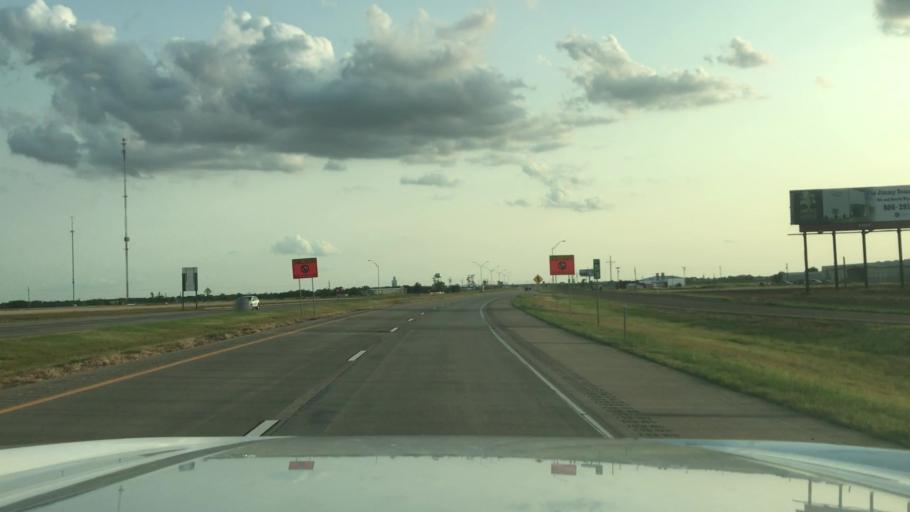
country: US
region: Texas
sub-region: Hale County
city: Seth Ward
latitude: 34.2318
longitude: -101.7113
